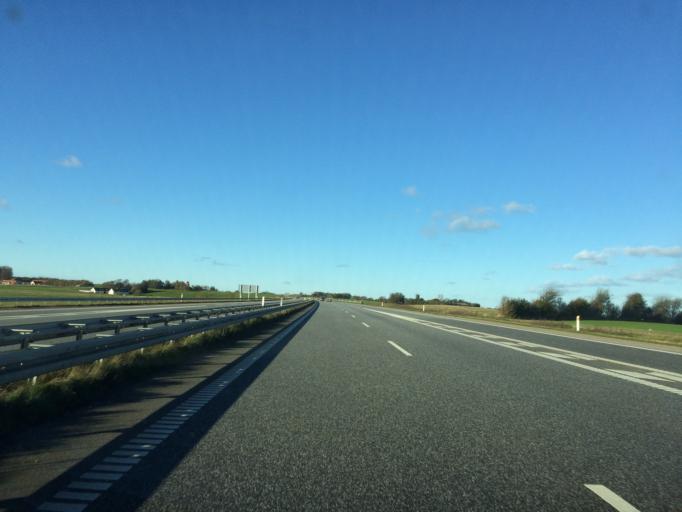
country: DK
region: Central Jutland
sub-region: Hedensted Kommune
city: Torring
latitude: 55.8058
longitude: 9.5610
